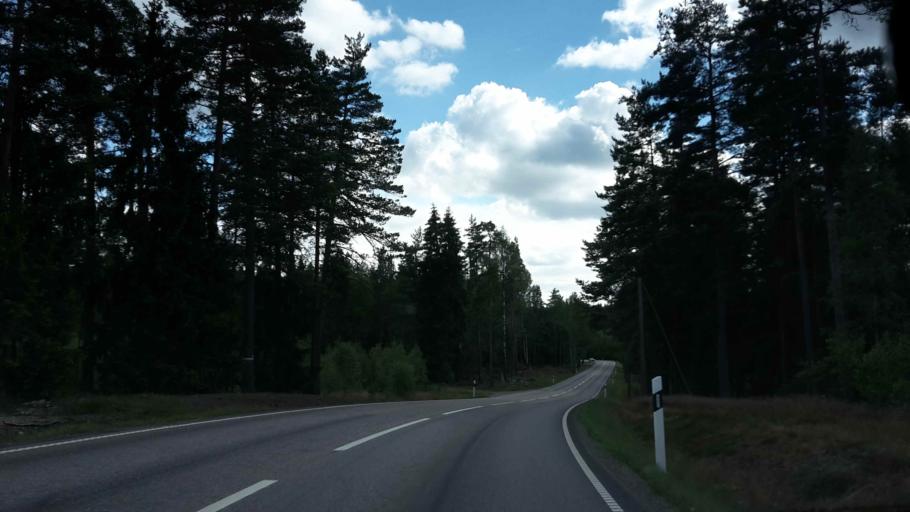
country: SE
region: OErebro
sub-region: Hallsbergs Kommun
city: Palsboda
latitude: 58.8323
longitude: 15.4107
